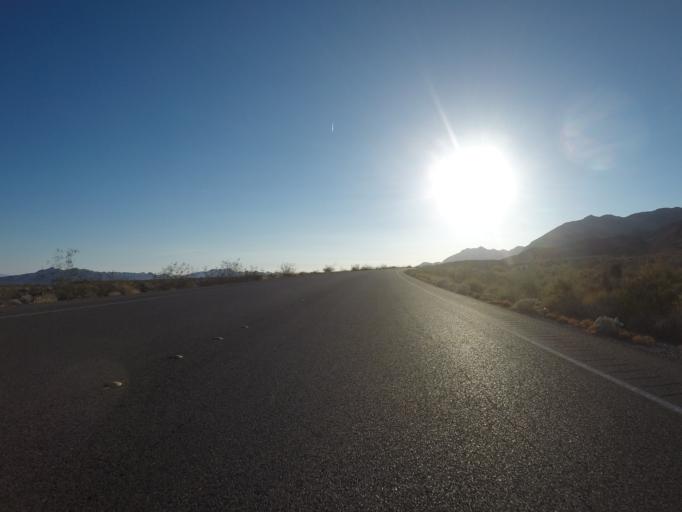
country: US
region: Nevada
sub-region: Clark County
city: Moapa Valley
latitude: 36.3821
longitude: -114.4353
